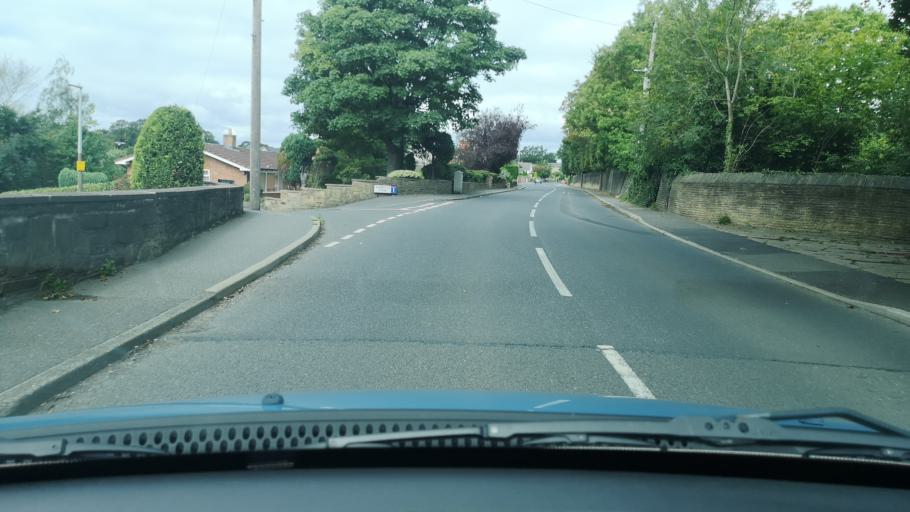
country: GB
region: England
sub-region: Kirklees
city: Mirfield
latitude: 53.6795
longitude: -1.6817
